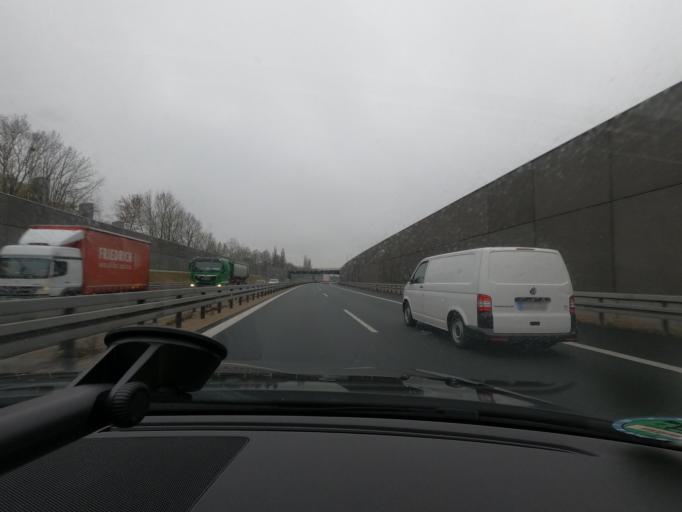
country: DE
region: Bavaria
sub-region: Upper Franconia
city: Forchheim
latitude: 49.7268
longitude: 11.0539
